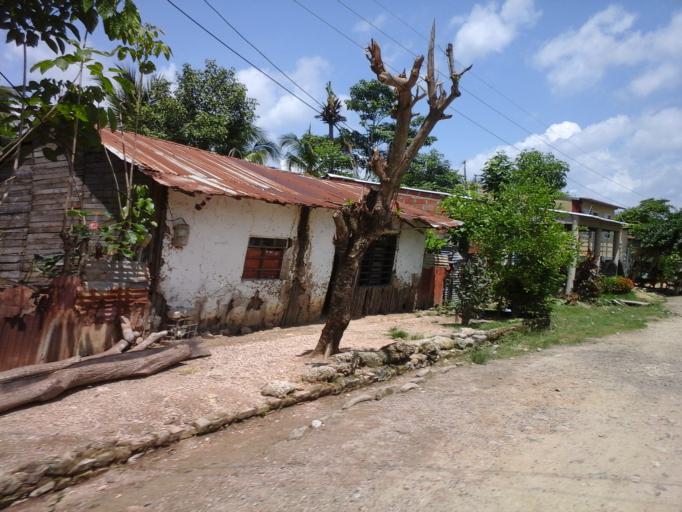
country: CO
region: Bolivar
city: San Pablo
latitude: 10.1484
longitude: -75.2769
